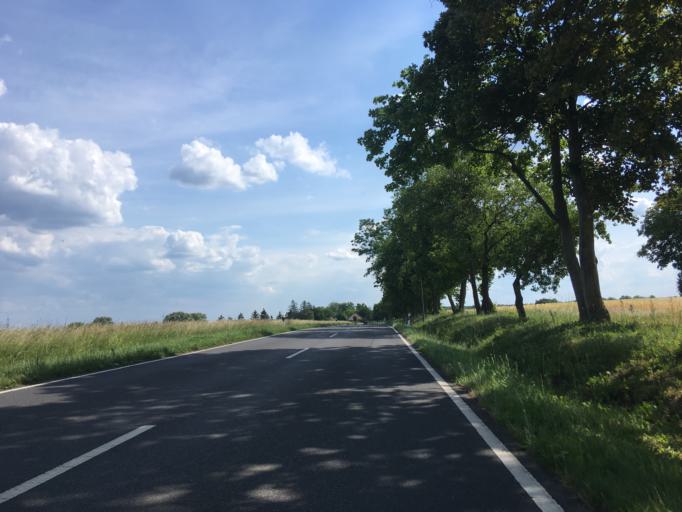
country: DE
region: Brandenburg
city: Muncheberg
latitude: 52.4415
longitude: 14.1015
